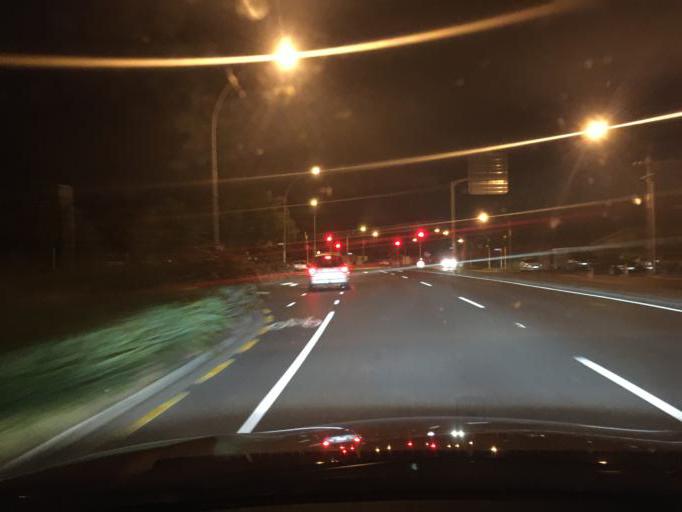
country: NZ
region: Waikato
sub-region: Hamilton City
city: Hamilton
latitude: -37.8079
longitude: 175.2862
